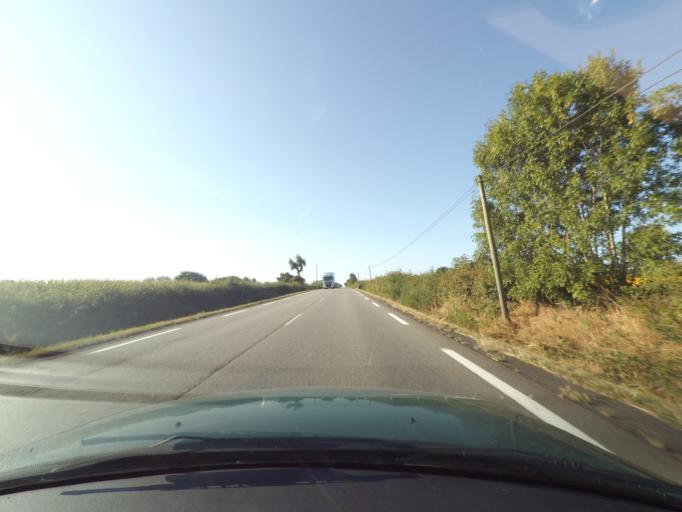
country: FR
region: Poitou-Charentes
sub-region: Departement des Deux-Sevres
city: Chiche
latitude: 46.7594
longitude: -0.3110
